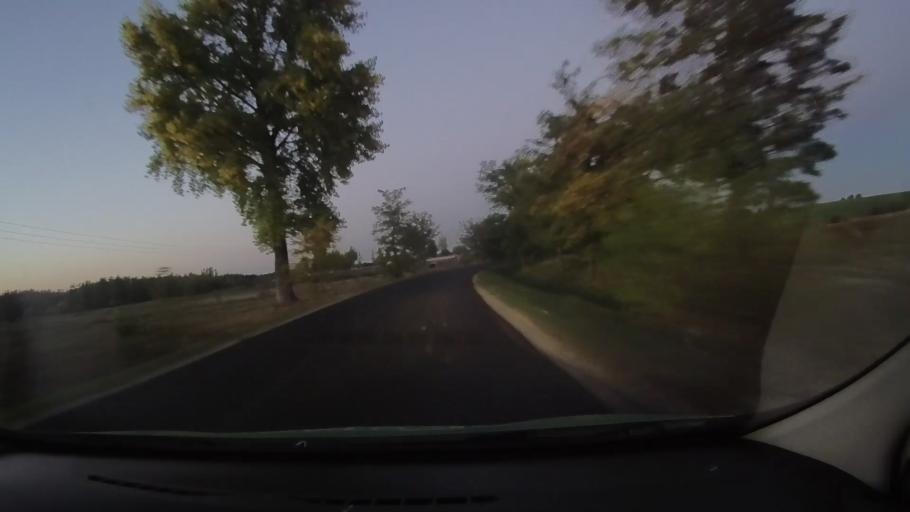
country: RO
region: Bihor
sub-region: Comuna Simian
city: Simian
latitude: 47.5071
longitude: 22.0948
